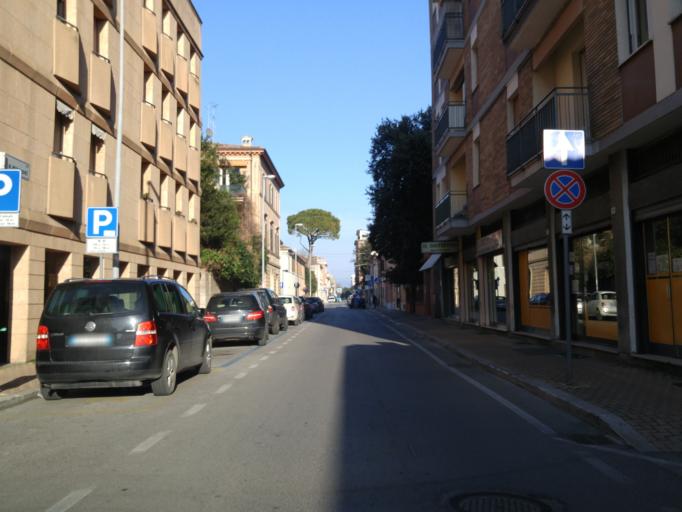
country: IT
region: The Marches
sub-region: Provincia di Pesaro e Urbino
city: Pesaro
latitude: 43.9070
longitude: 12.9146
